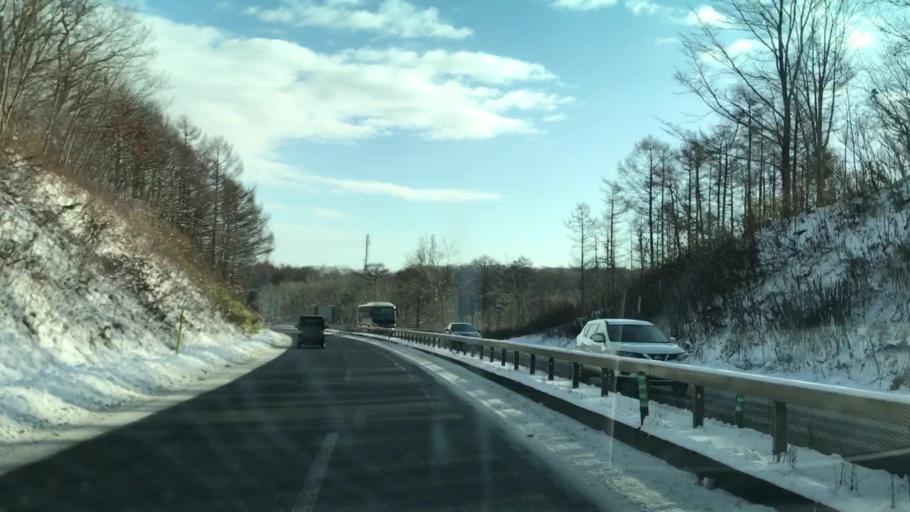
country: JP
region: Hokkaido
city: Chitose
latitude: 42.8103
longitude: 141.6295
